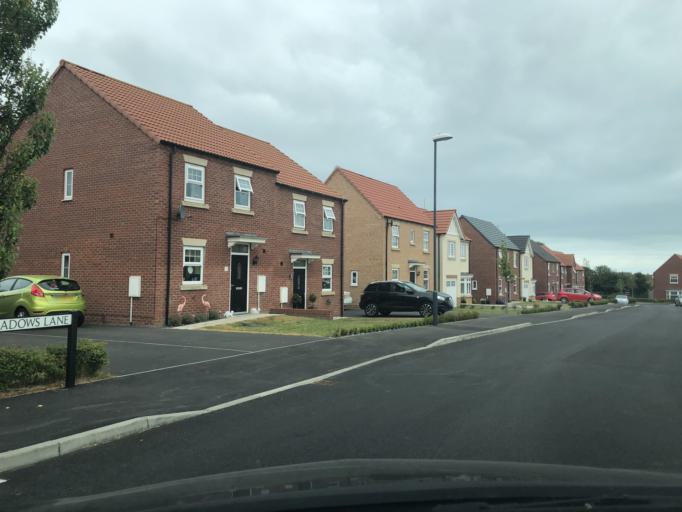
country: GB
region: England
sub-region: North Yorkshire
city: Filey
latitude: 54.2043
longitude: -0.2993
